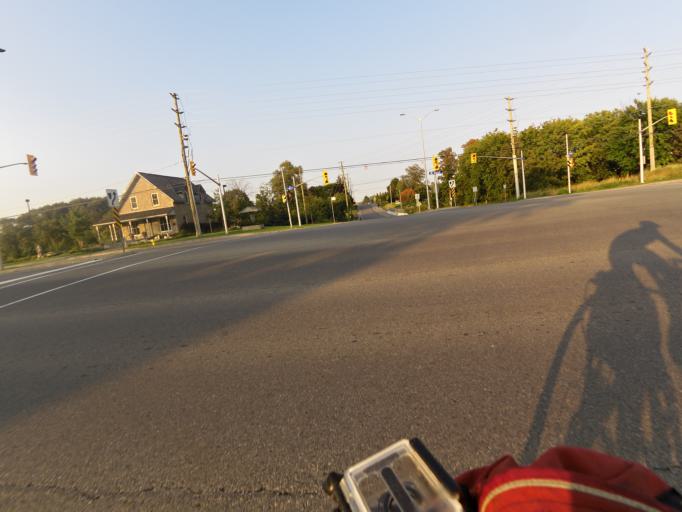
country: CA
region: Ontario
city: Bells Corners
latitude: 45.3551
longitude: -75.9325
